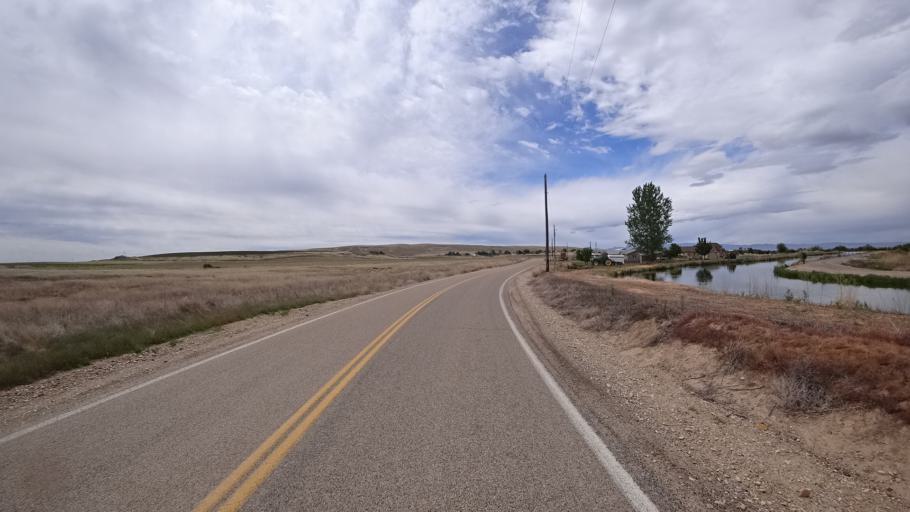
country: US
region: Idaho
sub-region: Ada County
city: Kuna
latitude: 43.4719
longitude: -116.4359
